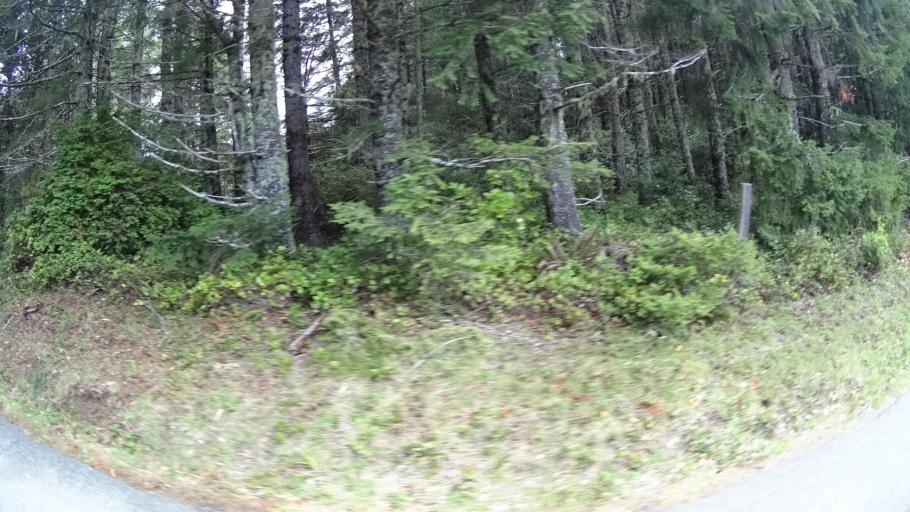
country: US
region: California
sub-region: Humboldt County
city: Blue Lake
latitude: 40.7930
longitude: -123.9714
